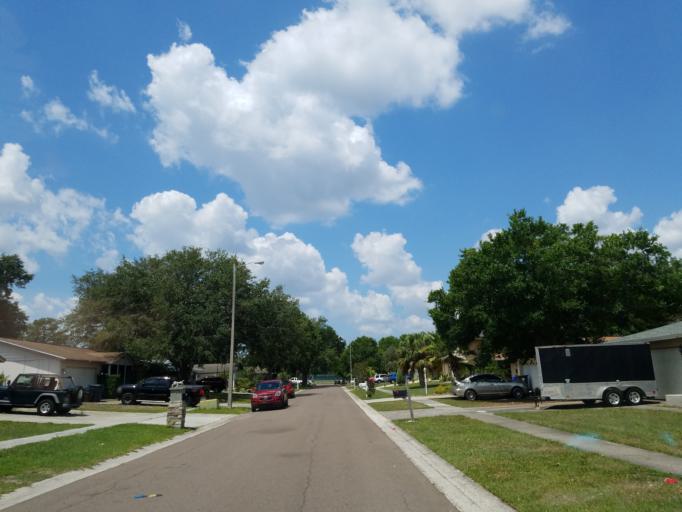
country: US
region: Florida
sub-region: Hillsborough County
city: Bloomingdale
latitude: 27.8827
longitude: -82.2712
